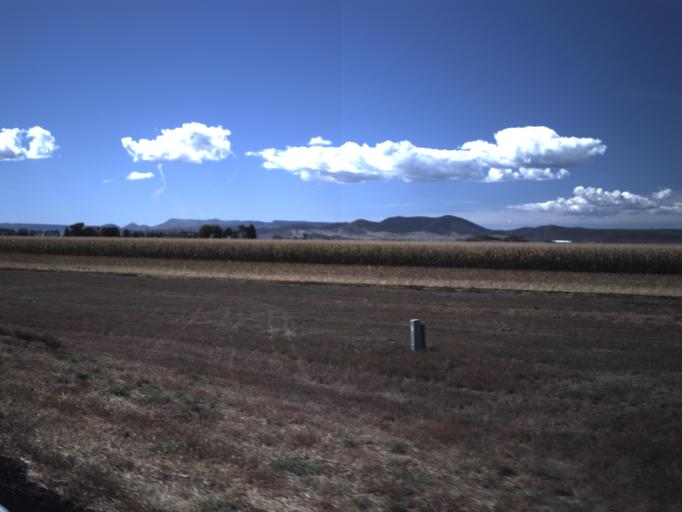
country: US
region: Utah
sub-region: Washington County
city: Enterprise
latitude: 37.7053
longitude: -113.6565
